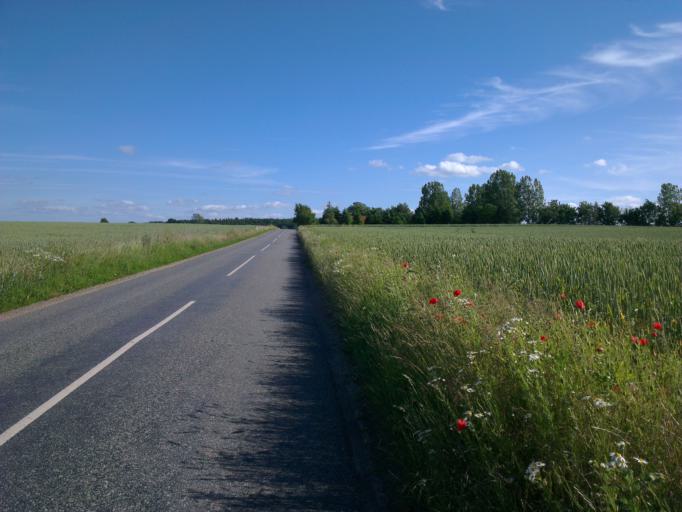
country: DK
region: Capital Region
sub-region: Frederikssund Kommune
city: Skibby
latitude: 55.8022
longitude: 11.9513
